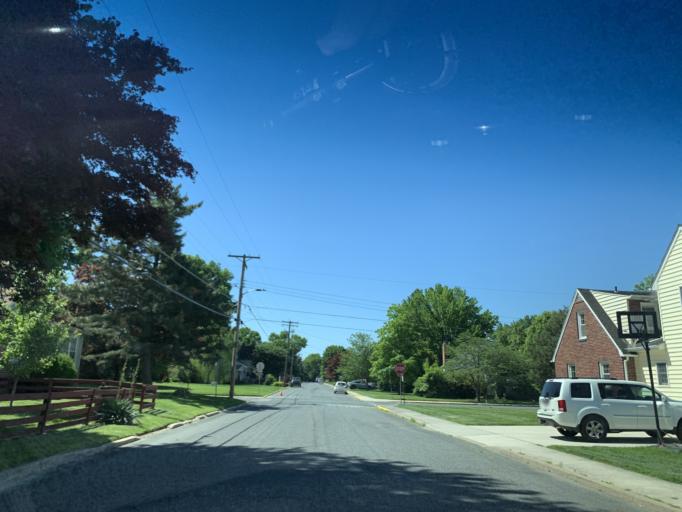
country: US
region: Maryland
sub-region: Harford County
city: Havre de Grace
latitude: 39.5418
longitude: -76.0951
